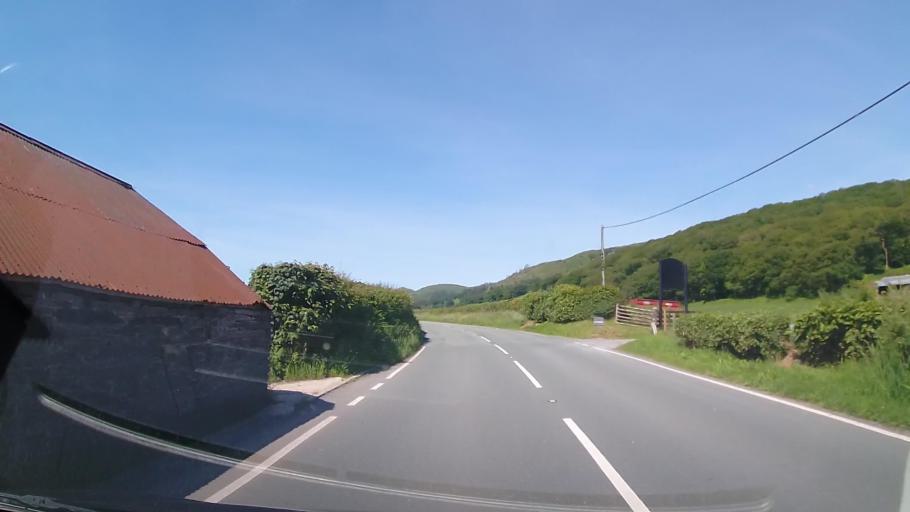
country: GB
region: Wales
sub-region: Sir Powys
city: Machynlleth
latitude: 52.5856
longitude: -3.9251
